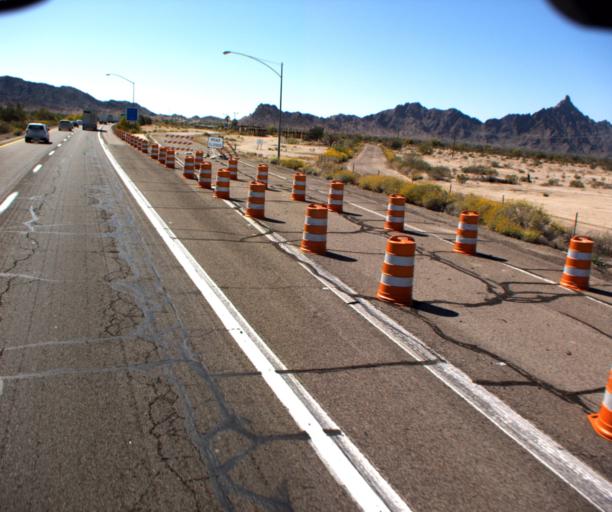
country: US
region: Arizona
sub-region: Yuma County
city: Wellton
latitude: 32.7321
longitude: -113.7118
